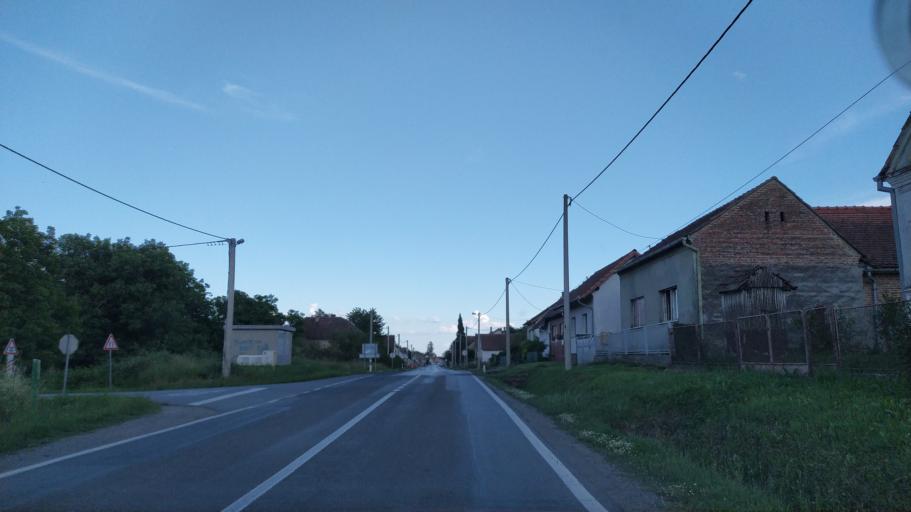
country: HR
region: Virovitick-Podravska
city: Slatina
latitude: 45.7411
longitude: 17.6058
